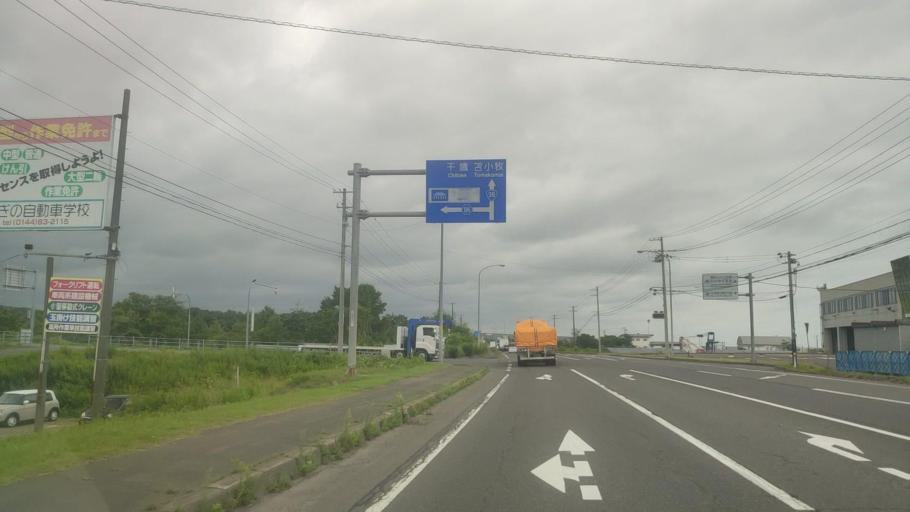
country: JP
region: Hokkaido
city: Shiraoi
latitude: 42.5265
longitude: 141.3190
